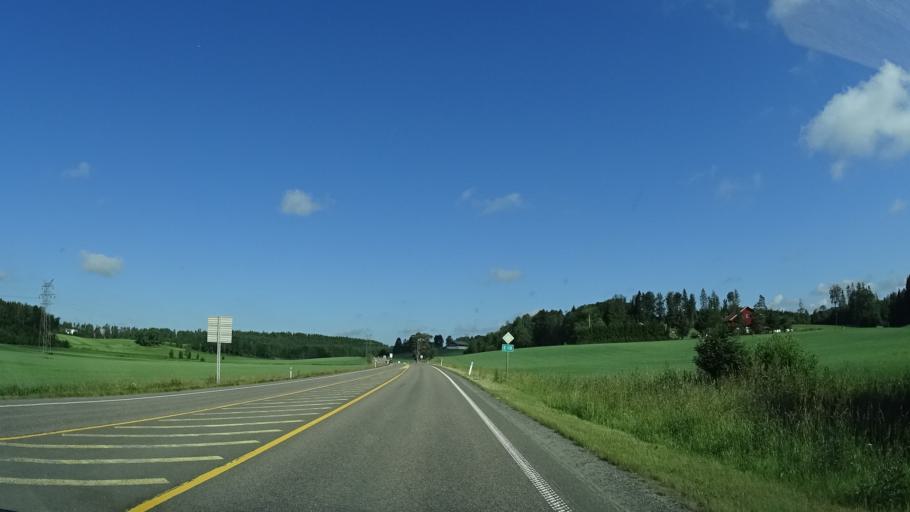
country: NO
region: Ostfold
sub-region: Hobol
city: Elvestad
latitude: 59.6555
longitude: 10.9180
